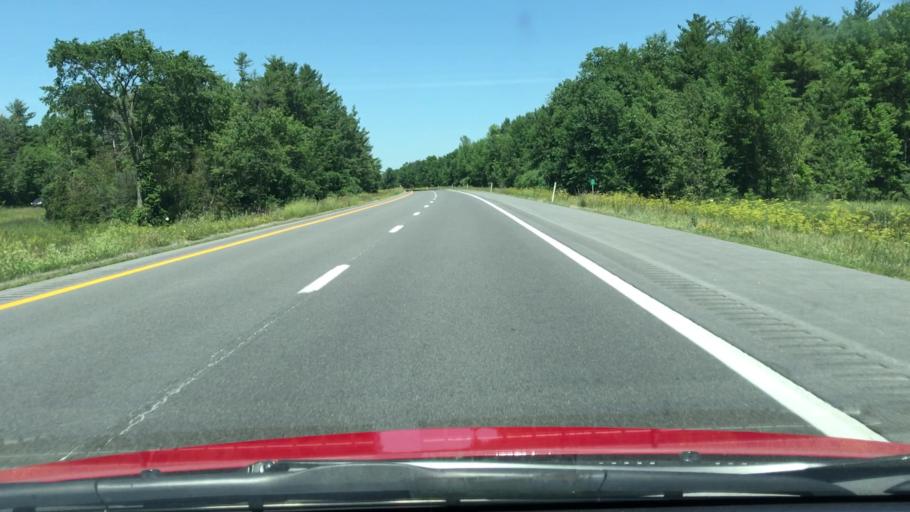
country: US
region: New York
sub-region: Clinton County
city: Cumberland Head
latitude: 44.8419
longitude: -73.4463
